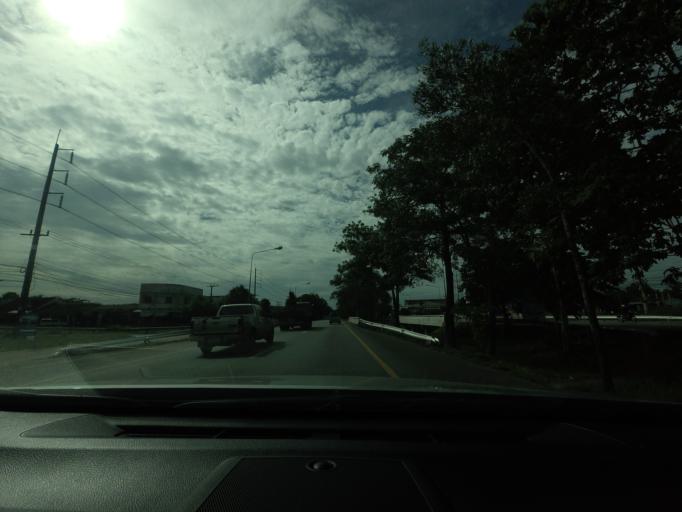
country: TH
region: Songkhla
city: Hat Yai
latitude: 6.9954
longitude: 100.4176
